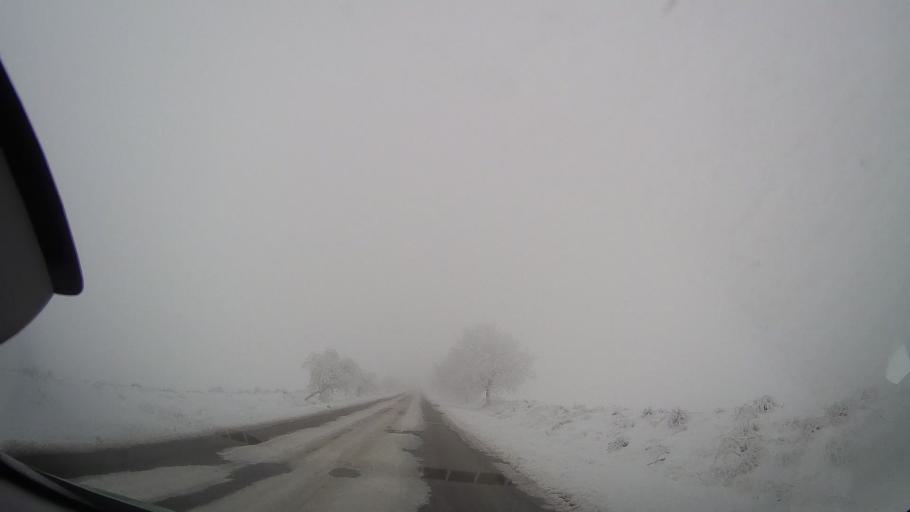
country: RO
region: Neamt
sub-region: Comuna Valea Ursului
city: Valea Ursului
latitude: 46.8190
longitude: 27.0646
